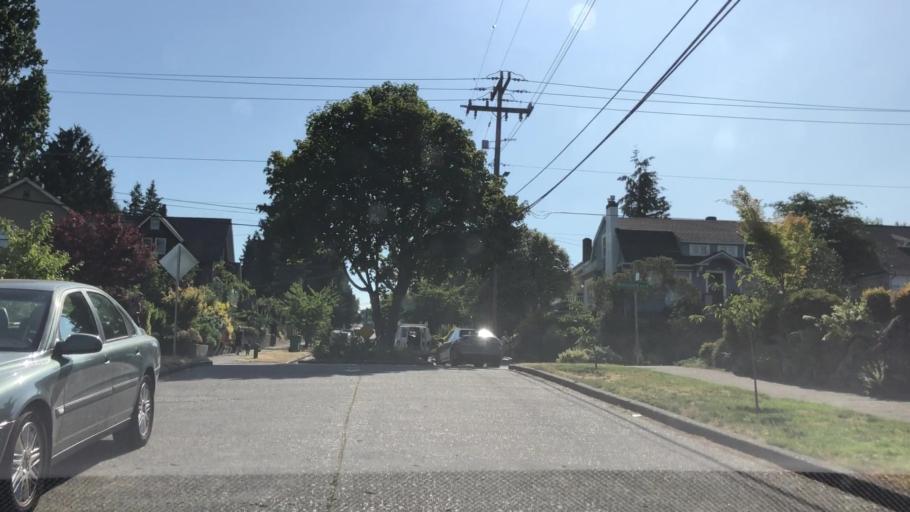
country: US
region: Washington
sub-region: King County
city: Seattle
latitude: 47.6687
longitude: -122.3368
